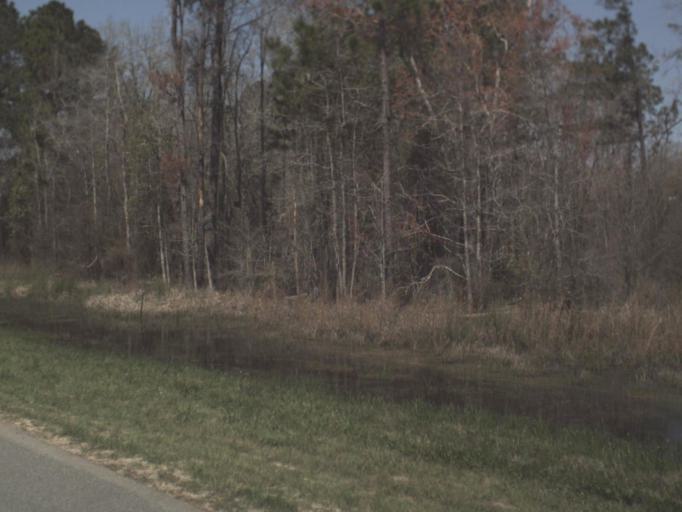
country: US
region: Alabama
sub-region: Geneva County
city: Geneva
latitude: 30.9413
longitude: -85.8175
